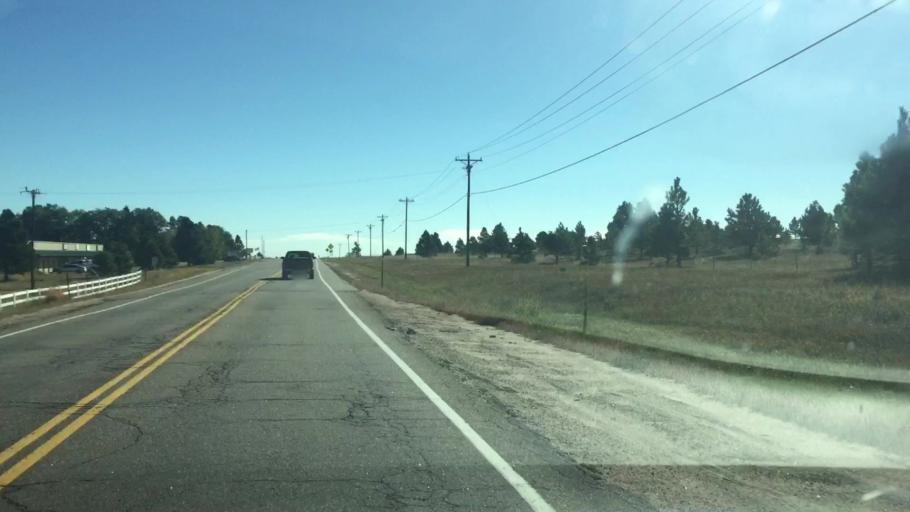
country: US
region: Colorado
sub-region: Elbert County
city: Elizabeth
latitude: 39.3613
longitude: -104.5662
